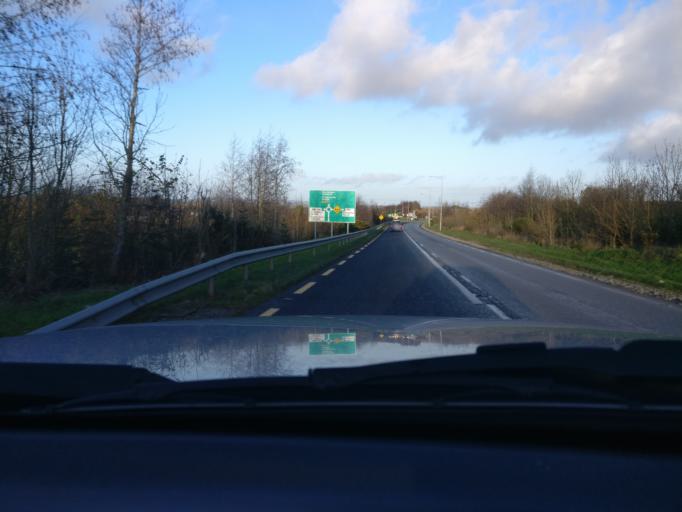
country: IE
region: Leinster
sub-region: An Mhi
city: Kells
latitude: 53.7304
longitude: -6.8934
